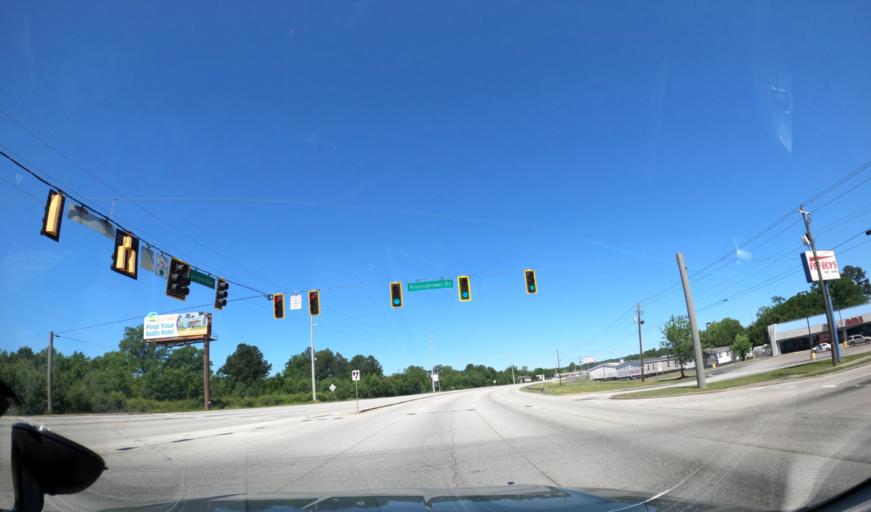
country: US
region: Georgia
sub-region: Richmond County
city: Augusta
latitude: 33.4401
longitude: -82.0268
